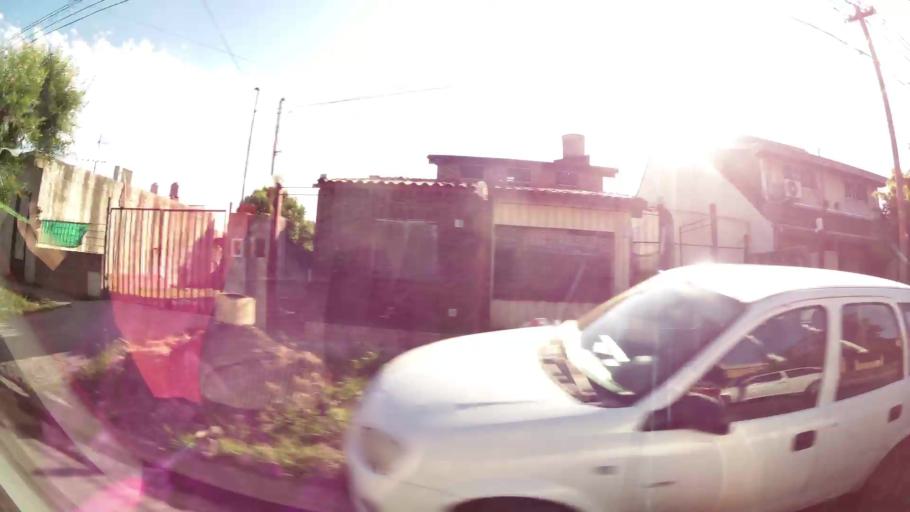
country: AR
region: Buenos Aires
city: Santa Catalina - Dique Lujan
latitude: -34.4853
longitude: -58.7284
